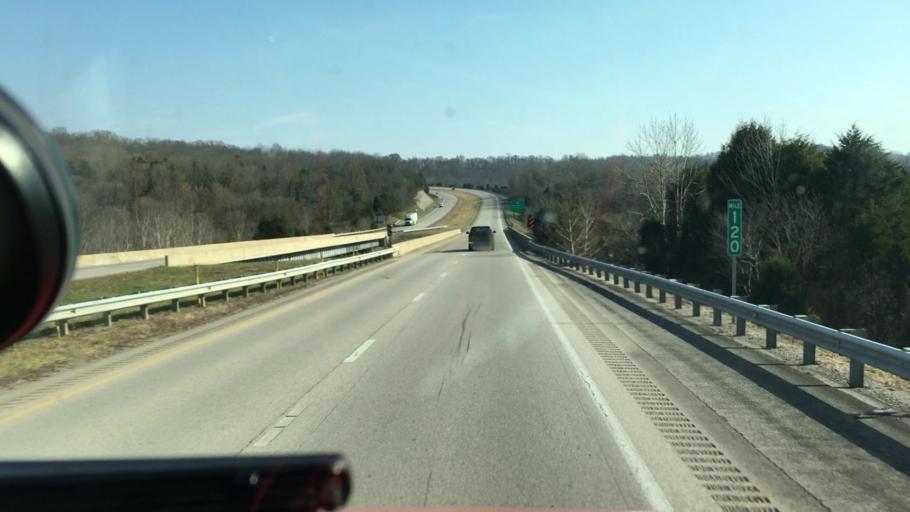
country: US
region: Kentucky
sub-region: Bath County
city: Owingsville
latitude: 38.1235
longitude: -83.7727
